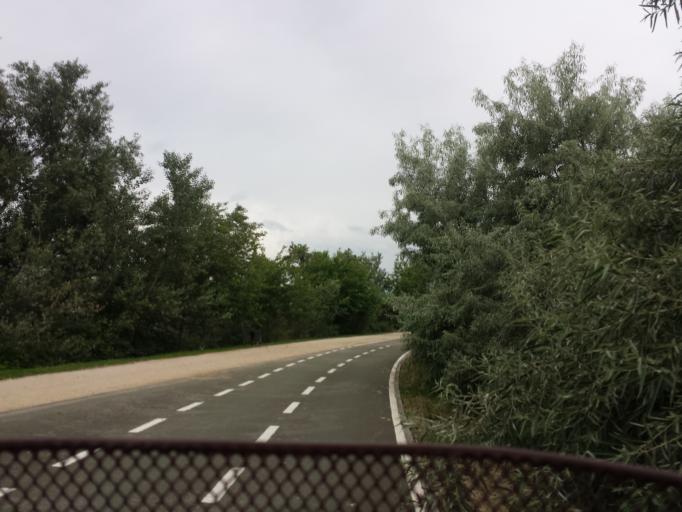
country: ES
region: Aragon
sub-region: Provincia de Zaragoza
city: Almozara
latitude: 41.6763
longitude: -0.9050
